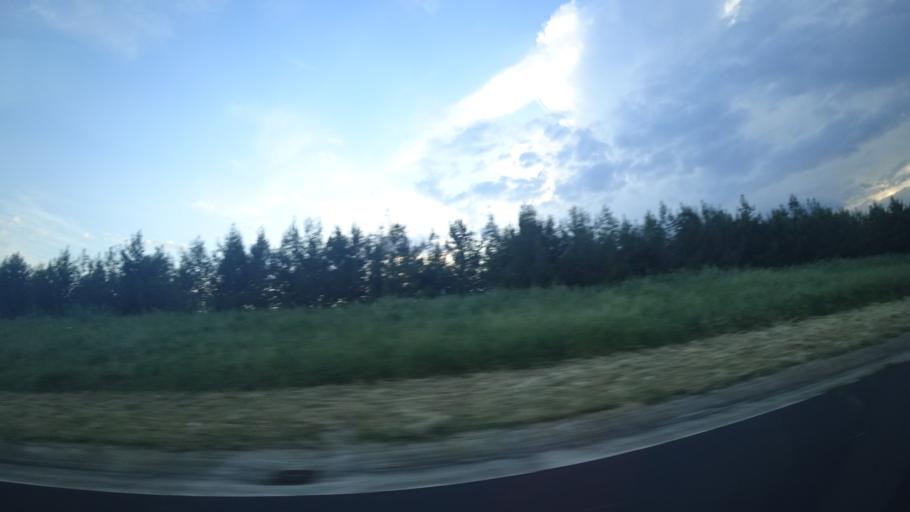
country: FR
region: Languedoc-Roussillon
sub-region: Departement de l'Herault
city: Aspiran
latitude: 43.5648
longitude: 3.4662
